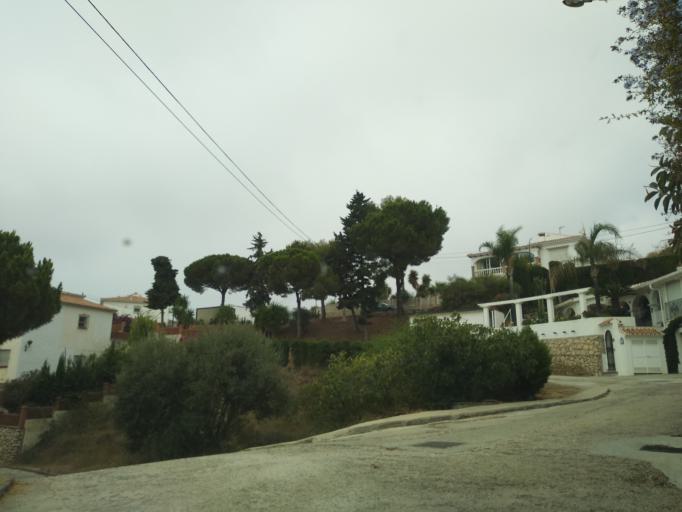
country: ES
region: Andalusia
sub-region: Provincia de Malaga
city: Iznate
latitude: 36.7196
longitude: -4.1891
